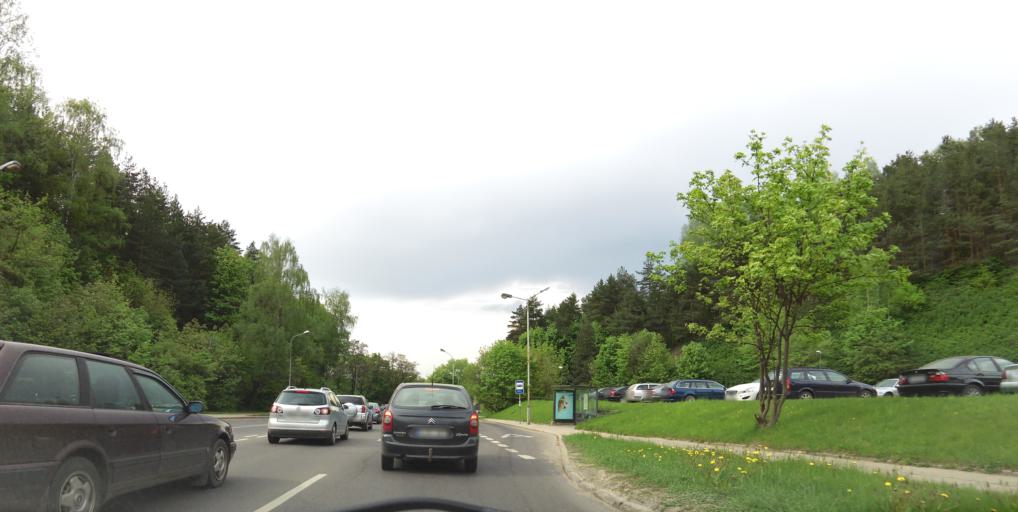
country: LT
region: Vilnius County
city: Rasos
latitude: 54.6877
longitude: 25.3055
